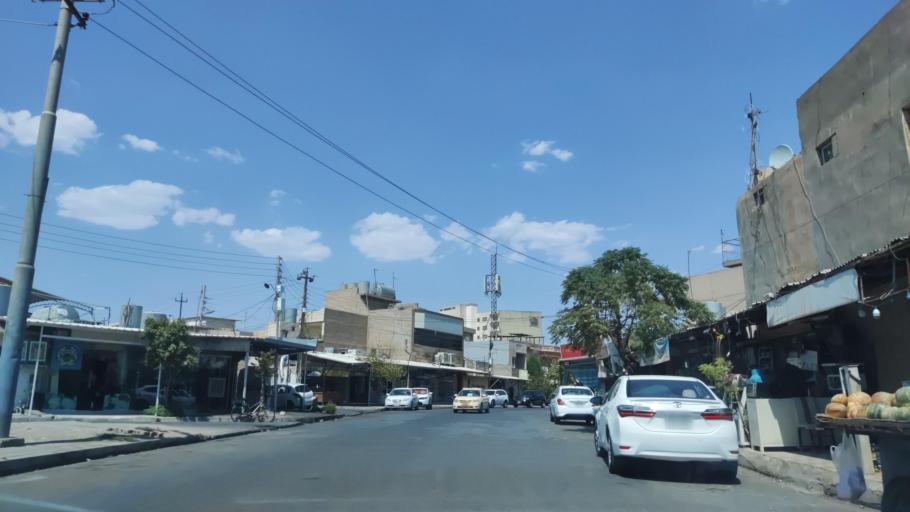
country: IQ
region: Arbil
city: Erbil
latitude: 36.1961
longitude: 44.0217
